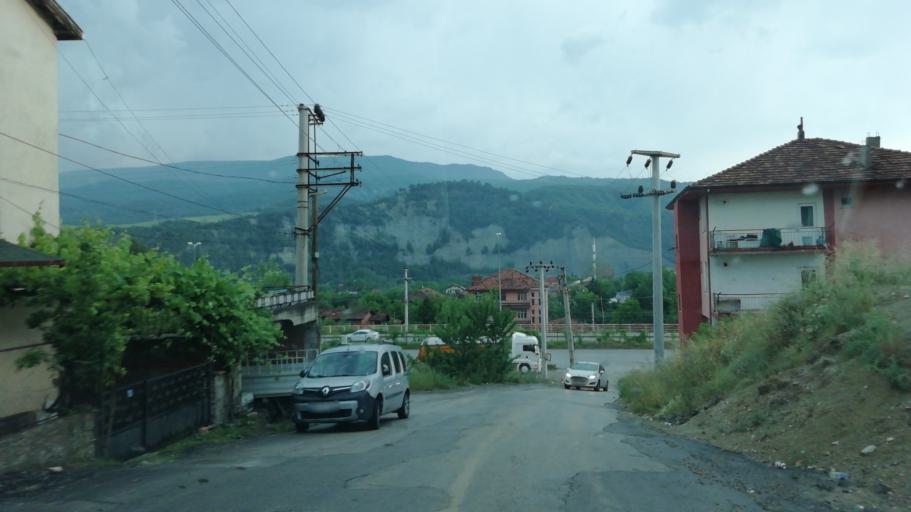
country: TR
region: Karabuk
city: Safranbolu
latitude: 41.2192
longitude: 32.6864
